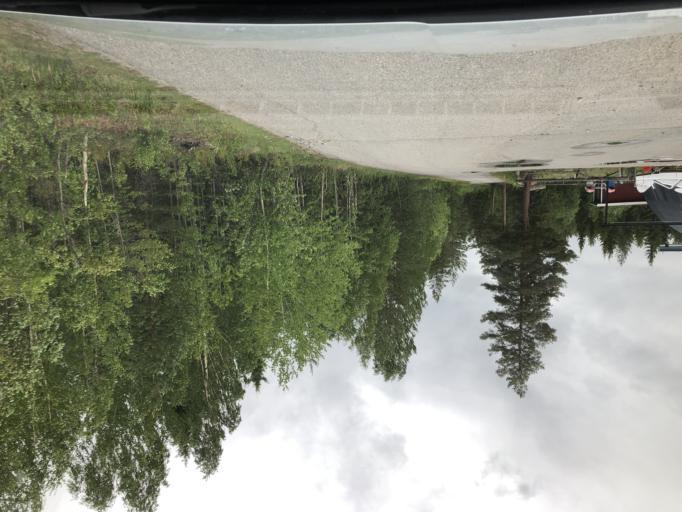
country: SE
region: Norrbotten
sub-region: Pitea Kommun
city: Roknas
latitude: 65.3918
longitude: 21.2695
